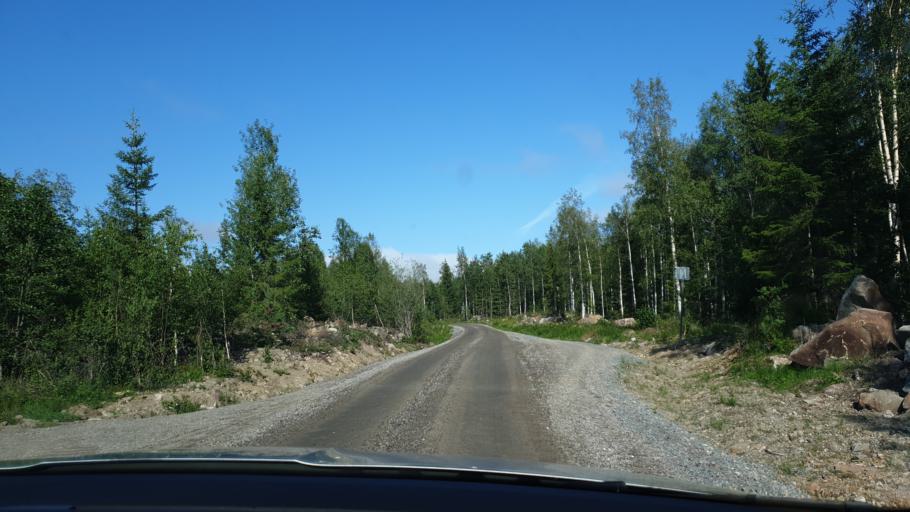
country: SE
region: Gaevleborg
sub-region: Soderhamns Kommun
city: Marielund
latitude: 61.4519
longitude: 17.0640
